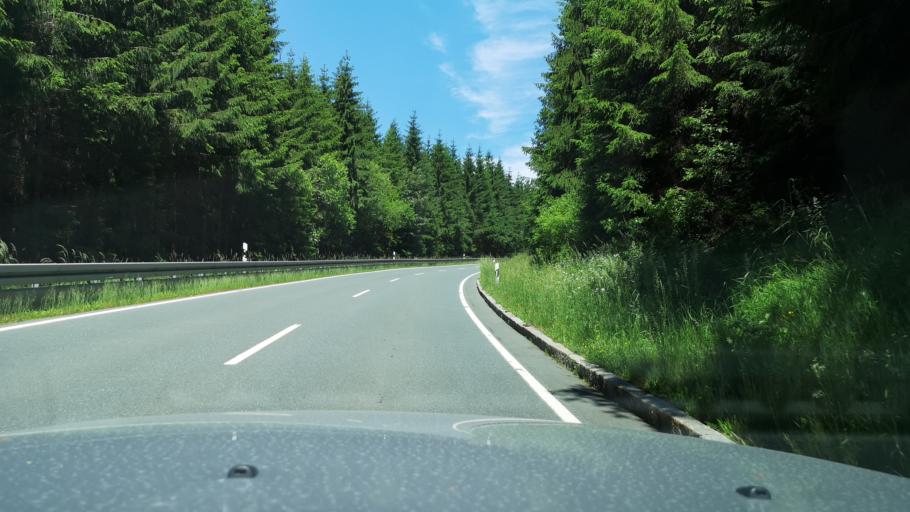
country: DE
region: Bavaria
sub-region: Upper Franconia
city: Tschirn
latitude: 50.4032
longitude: 11.4664
